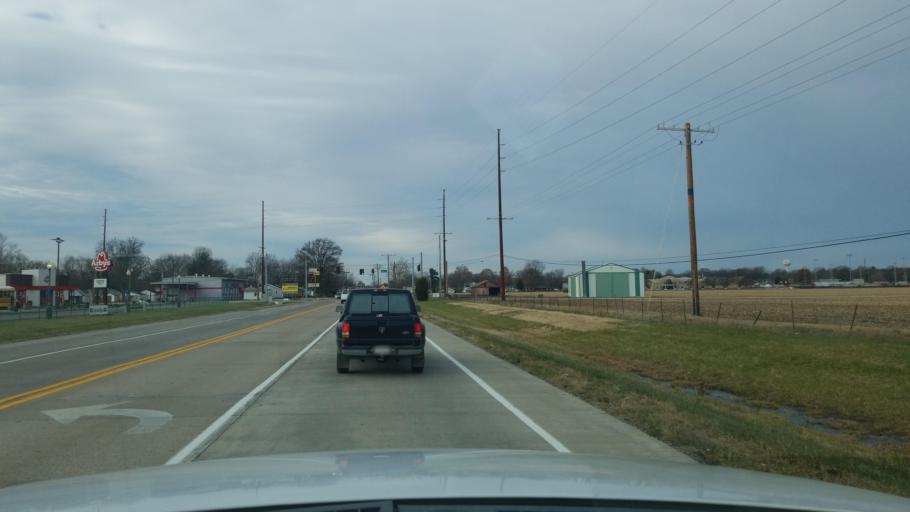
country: US
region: Indiana
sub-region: Posey County
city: Mount Vernon
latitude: 37.9370
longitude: -87.8772
